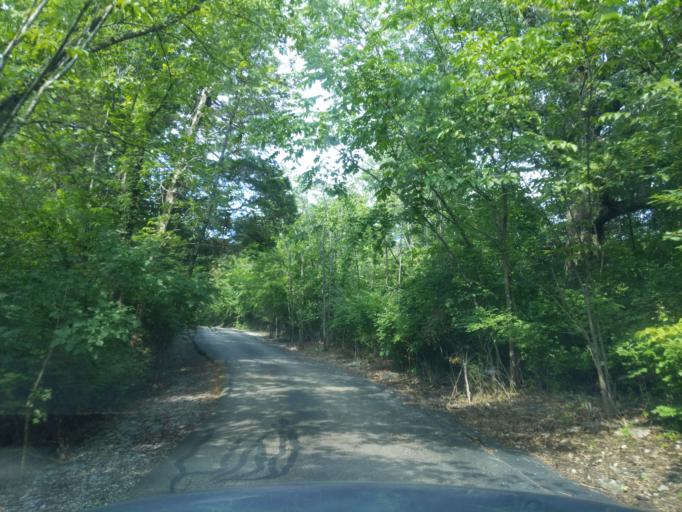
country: US
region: Tennessee
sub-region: Williamson County
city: Brentwood Estates
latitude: 36.0111
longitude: -86.7581
